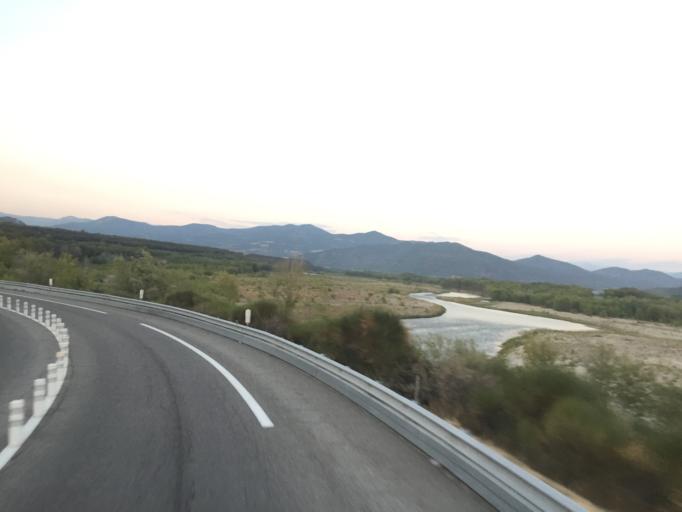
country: FR
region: Provence-Alpes-Cote d'Azur
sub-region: Departement des Alpes-de-Haute-Provence
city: Les Mees
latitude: 44.0395
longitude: 5.9671
